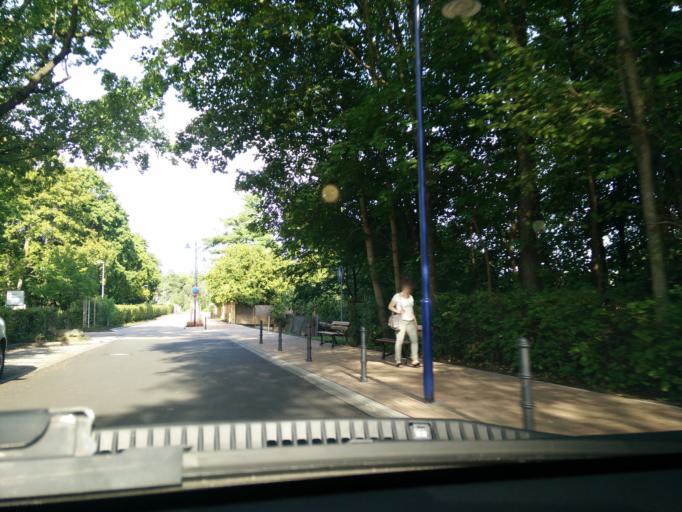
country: DE
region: Saxony
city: Bad Lausick
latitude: 51.1480
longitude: 12.6511
